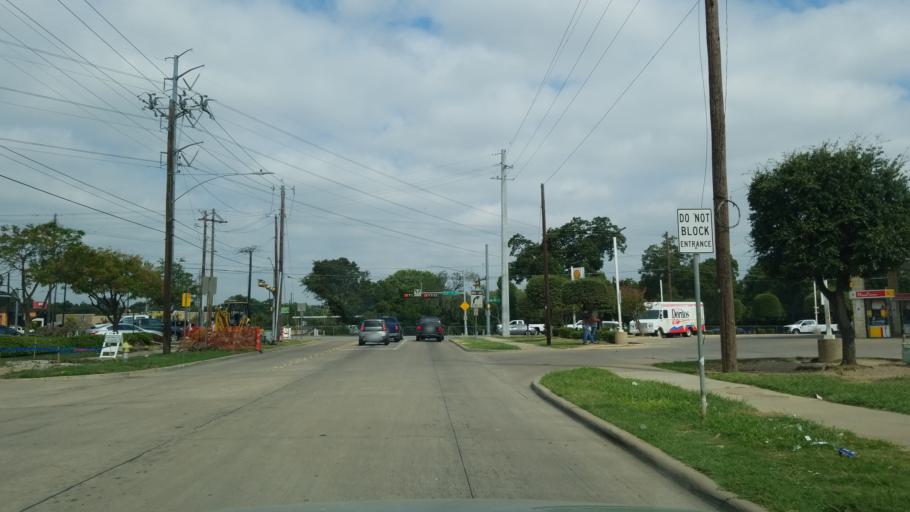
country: US
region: Texas
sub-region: Dallas County
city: Garland
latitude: 32.8936
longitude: -96.6482
